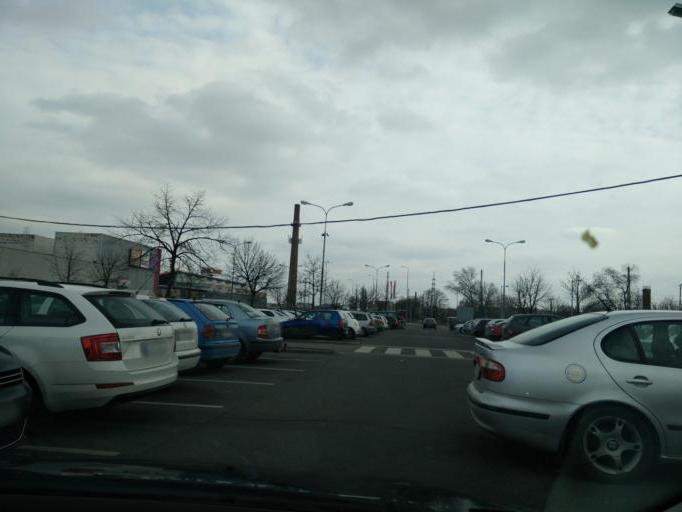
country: HU
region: Gyor-Moson-Sopron
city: Gyor
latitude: 47.6876
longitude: 17.6482
